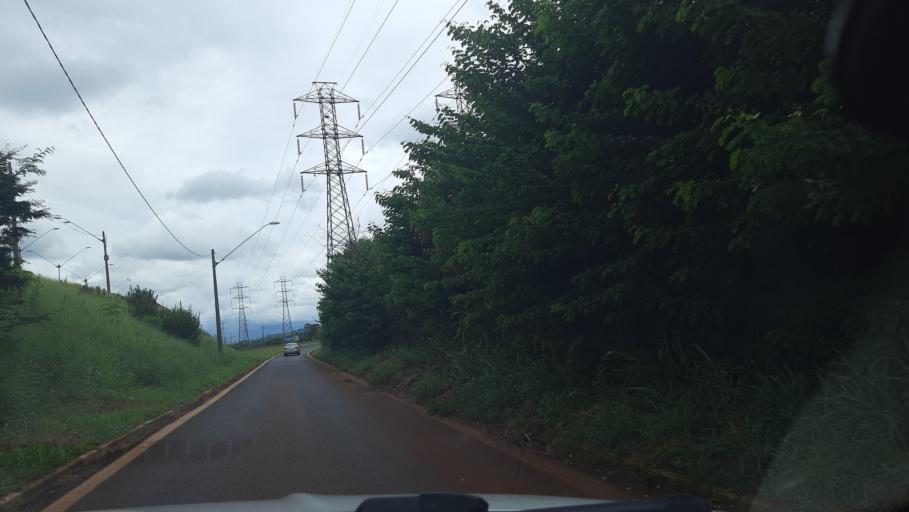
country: BR
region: Sao Paulo
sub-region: Ribeirao Preto
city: Ribeirao Preto
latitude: -21.2142
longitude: -47.7738
